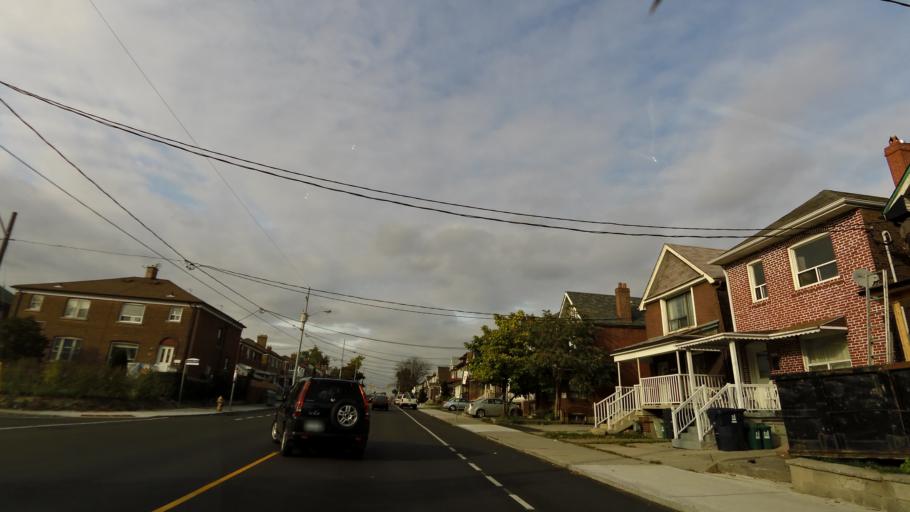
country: CA
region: Ontario
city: Toronto
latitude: 43.6835
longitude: -79.4372
